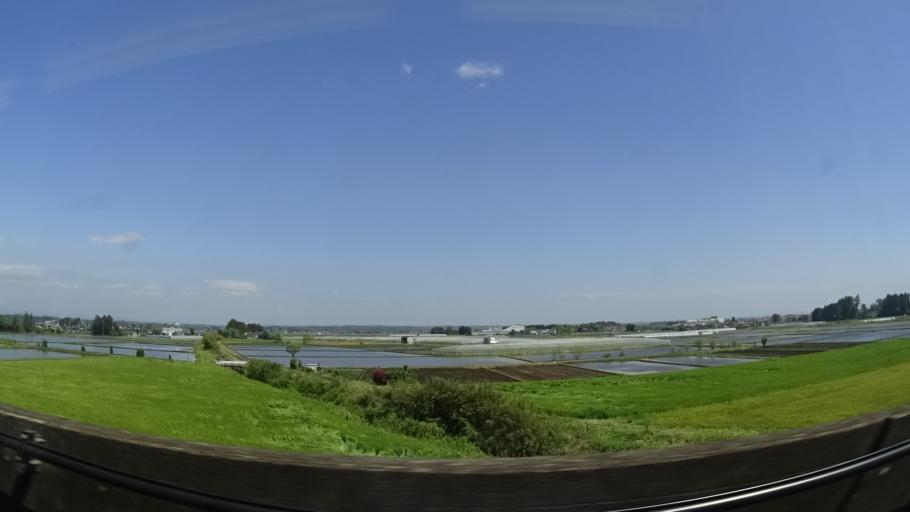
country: JP
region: Tochigi
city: Ujiie
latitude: 36.7230
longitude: 139.9278
